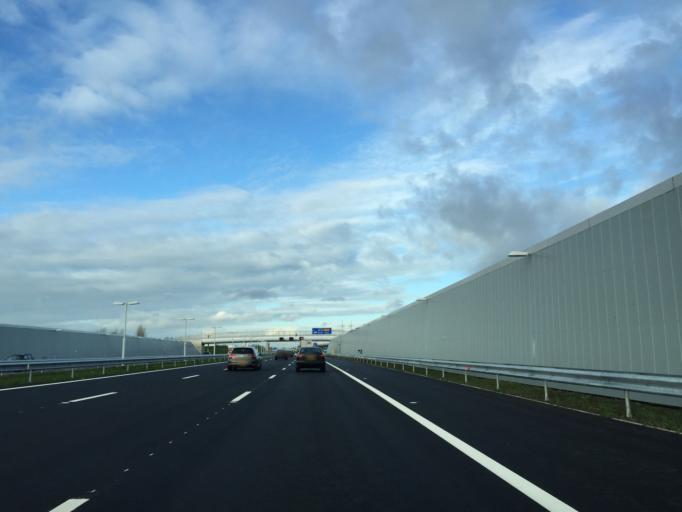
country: NL
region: South Holland
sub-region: Gemeente Delft
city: Delft
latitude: 51.9724
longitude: 4.3395
